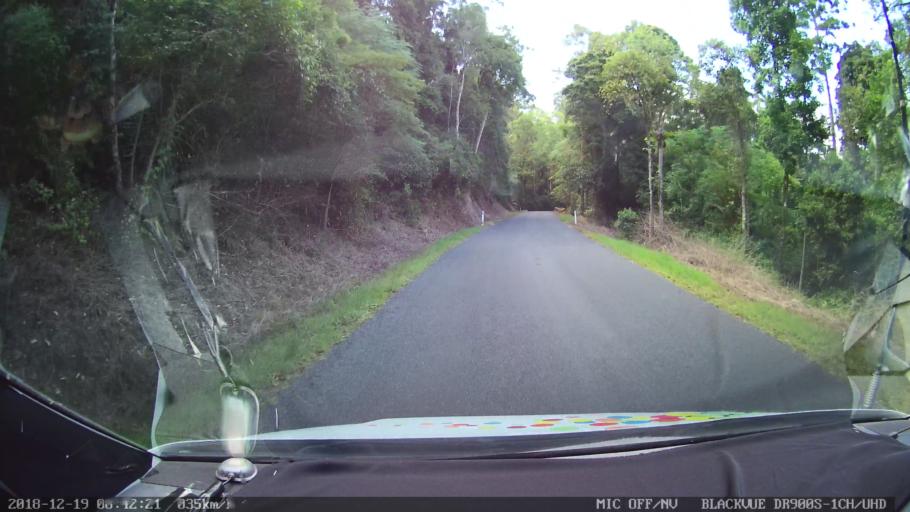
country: AU
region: New South Wales
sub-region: Kyogle
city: Kyogle
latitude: -28.3442
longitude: 152.9721
